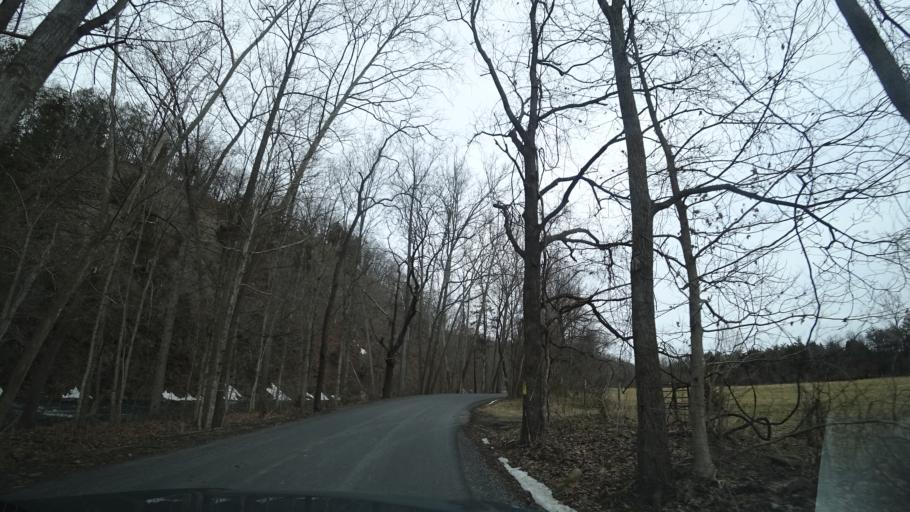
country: US
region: Virginia
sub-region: Shenandoah County
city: Woodstock
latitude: 39.0656
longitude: -78.6303
